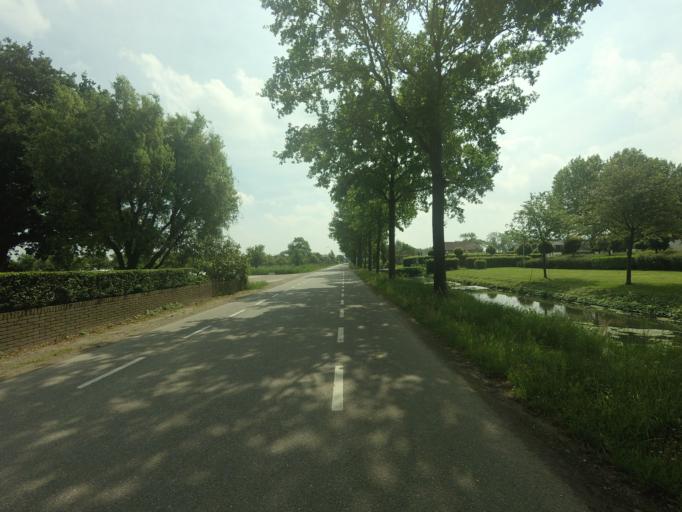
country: NL
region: Utrecht
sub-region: Gemeente Vianen
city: Vianen
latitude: 52.0064
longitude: 5.1240
